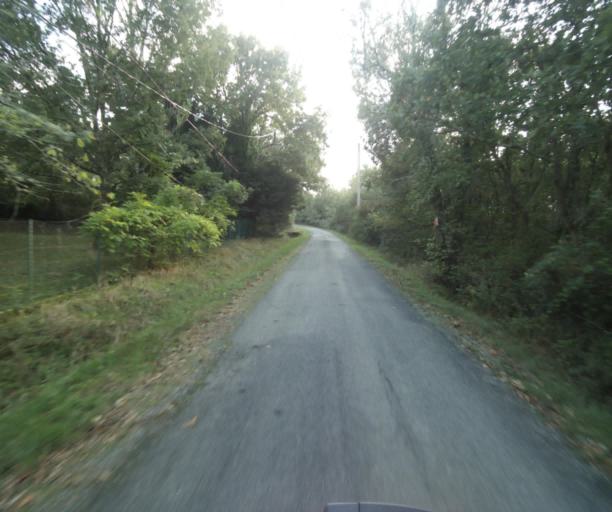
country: FR
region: Midi-Pyrenees
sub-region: Departement de la Haute-Garonne
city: Launac
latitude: 43.8136
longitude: 1.1323
